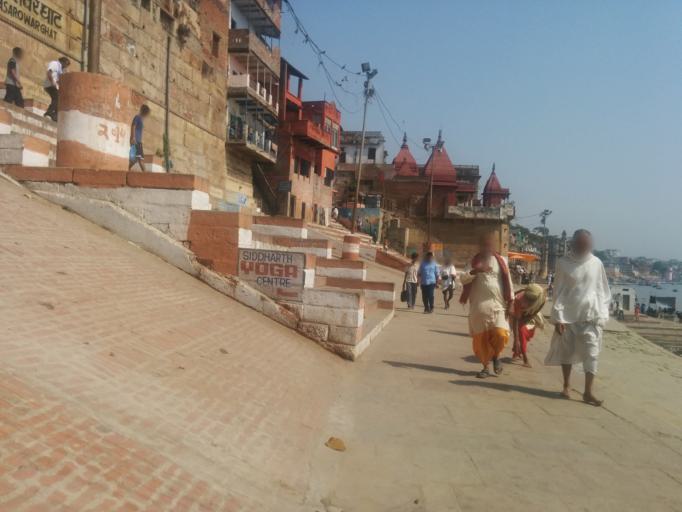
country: IN
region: Uttar Pradesh
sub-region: Varanasi
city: Varanasi
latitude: 25.3017
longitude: 83.0077
